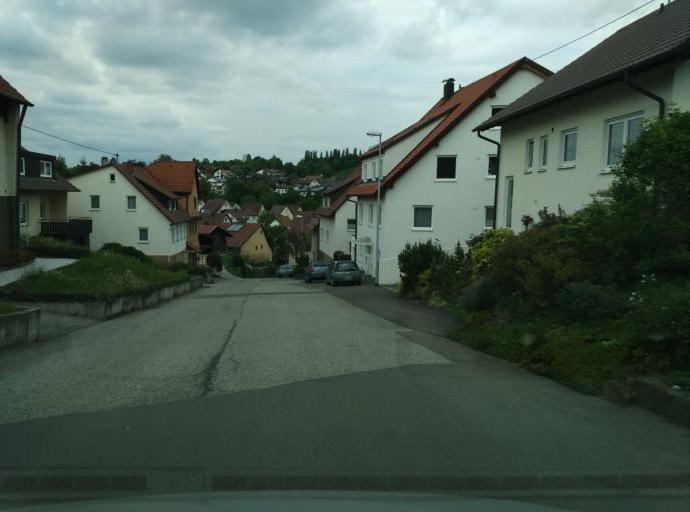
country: DE
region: Baden-Wuerttemberg
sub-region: Regierungsbezirk Stuttgart
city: Neuffen
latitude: 48.5515
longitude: 9.3767
